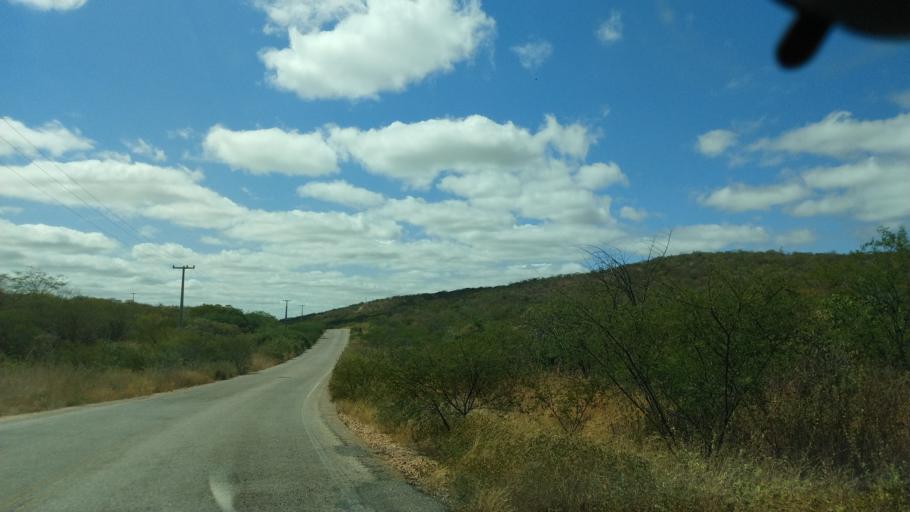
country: BR
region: Rio Grande do Norte
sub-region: Currais Novos
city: Currais Novos
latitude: -6.2619
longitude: -36.5835
